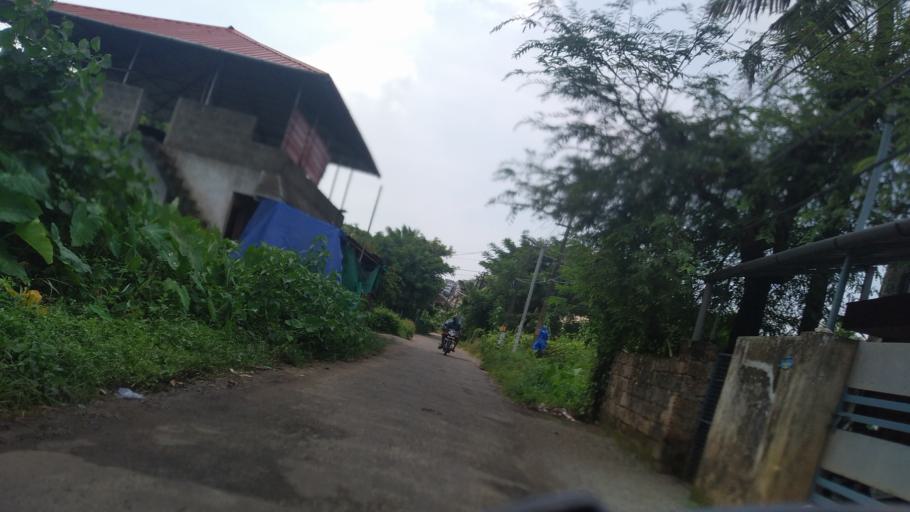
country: IN
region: Kerala
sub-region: Ernakulam
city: Cochin
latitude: 9.9786
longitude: 76.3062
